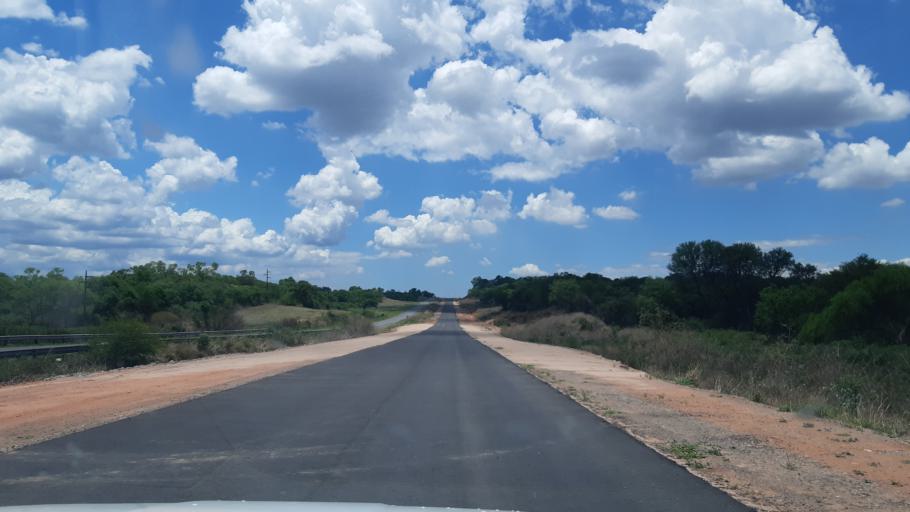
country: AR
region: Jujuy
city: La Mendieta
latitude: -24.4080
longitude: -64.9946
